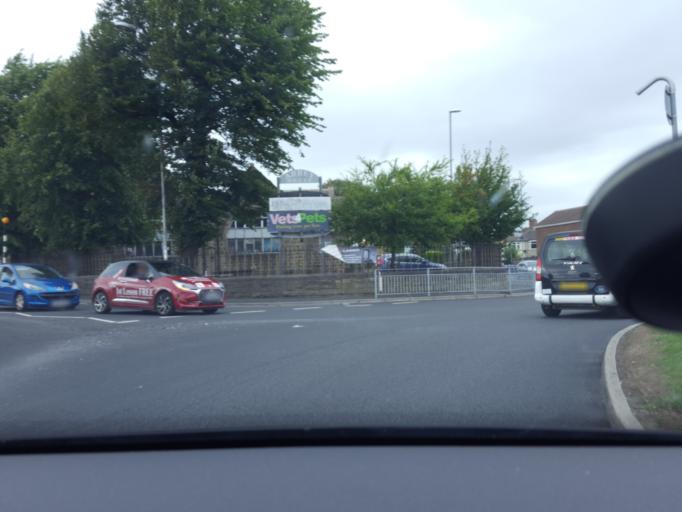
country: GB
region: England
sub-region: City and Borough of Leeds
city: Horsforth
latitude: 53.8053
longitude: -1.6227
